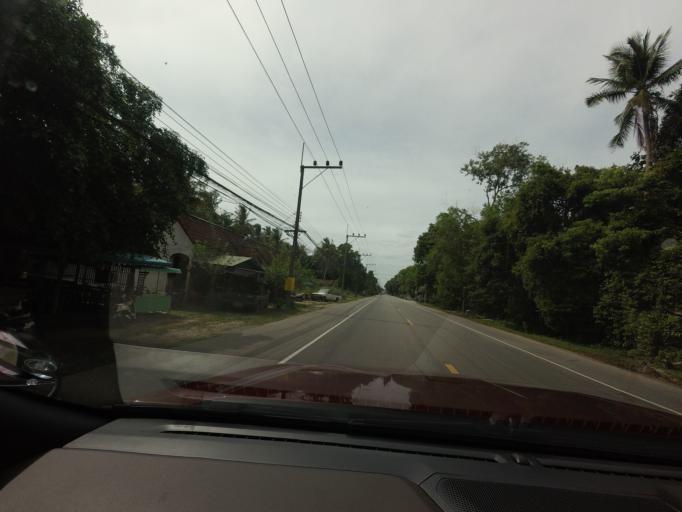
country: TH
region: Narathiwat
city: Tak Bai
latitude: 6.2460
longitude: 102.0724
